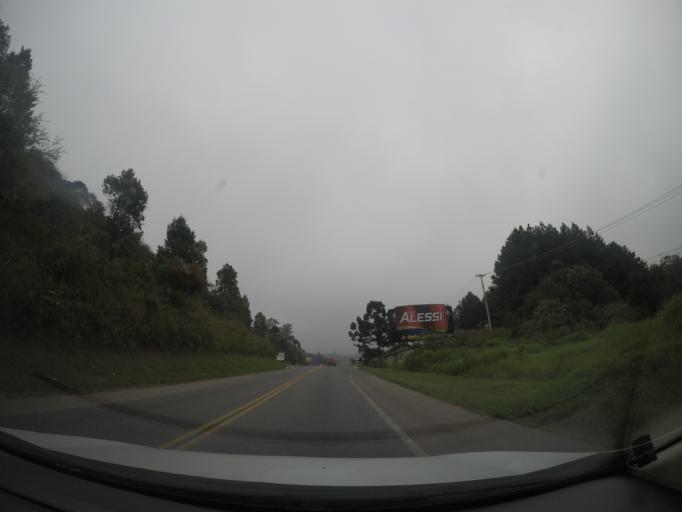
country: BR
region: Parana
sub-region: Almirante Tamandare
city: Almirante Tamandare
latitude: -25.3258
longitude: -49.2963
